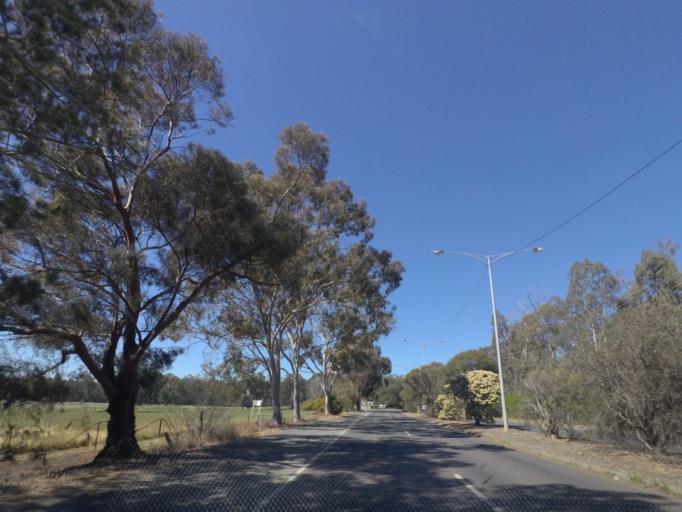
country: AU
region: Victoria
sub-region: Murrindindi
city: Kinglake West
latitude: -37.0217
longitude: 145.1180
